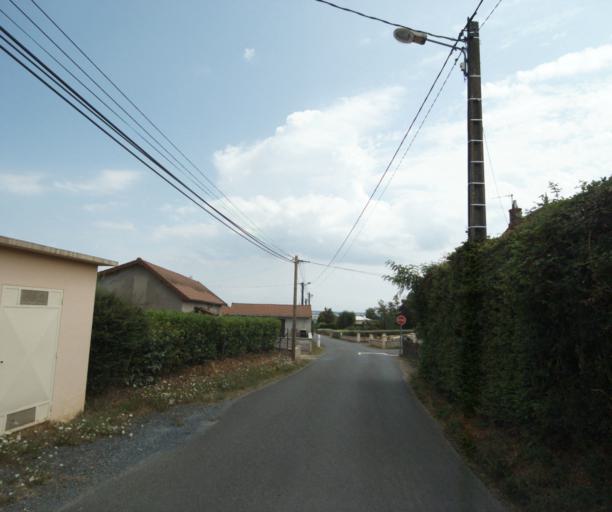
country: FR
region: Bourgogne
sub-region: Departement de Saone-et-Loire
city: Gueugnon
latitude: 46.5990
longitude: 4.0294
